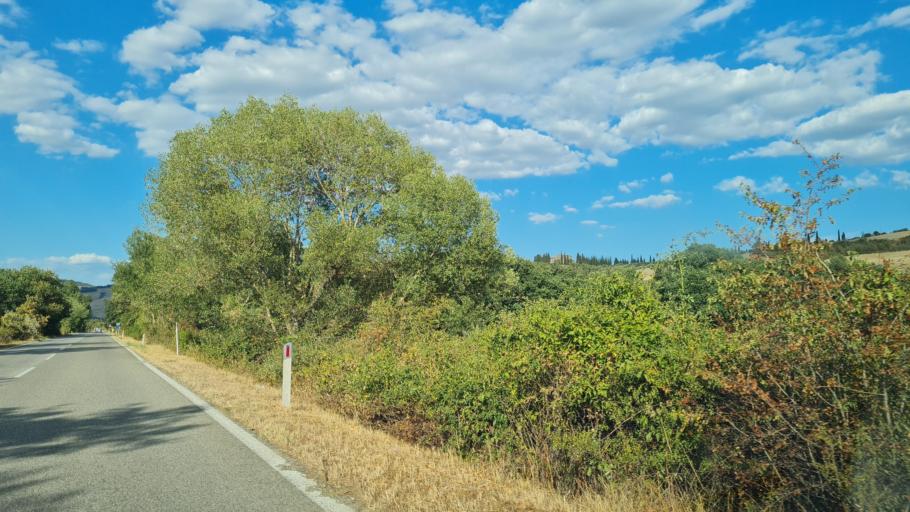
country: IT
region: Tuscany
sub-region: Provincia di Siena
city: Pienza
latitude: 42.9922
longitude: 11.7199
